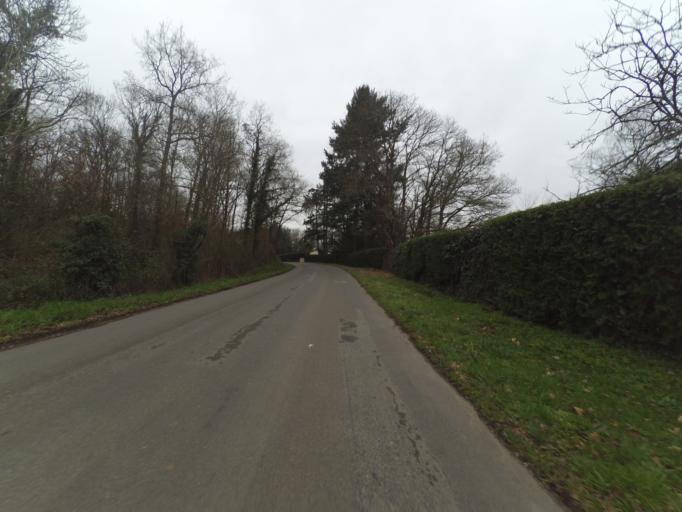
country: FR
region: Pays de la Loire
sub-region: Departement de la Loire-Atlantique
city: Coueron
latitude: 47.2329
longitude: -1.6939
